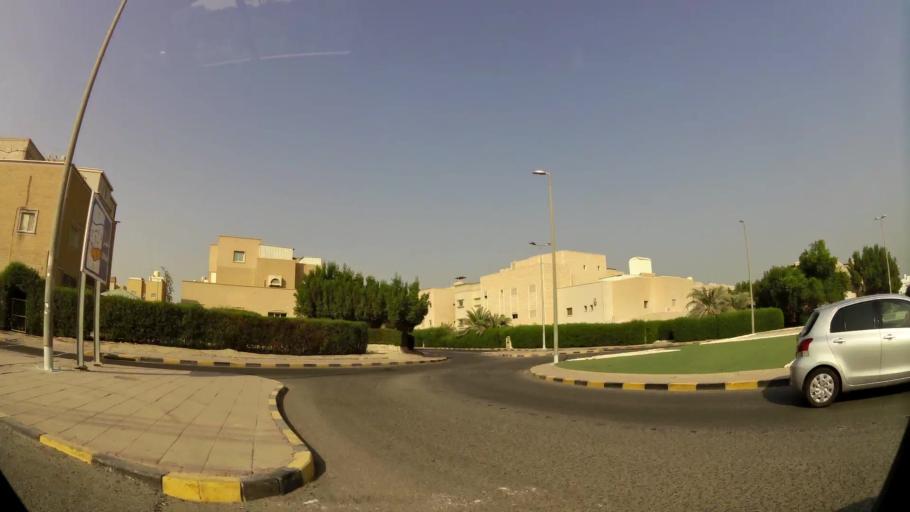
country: KW
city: Al Funaytis
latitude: 29.2155
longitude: 48.0827
